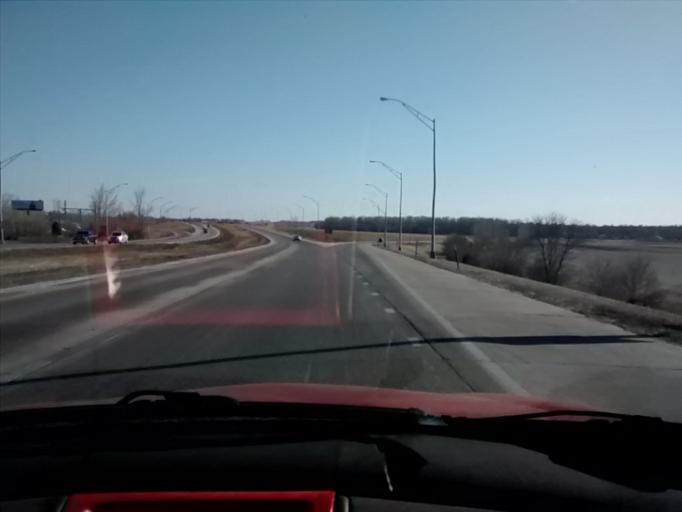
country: US
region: Nebraska
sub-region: Sarpy County
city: Offutt Air Force Base
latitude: 41.1460
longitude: -95.9389
